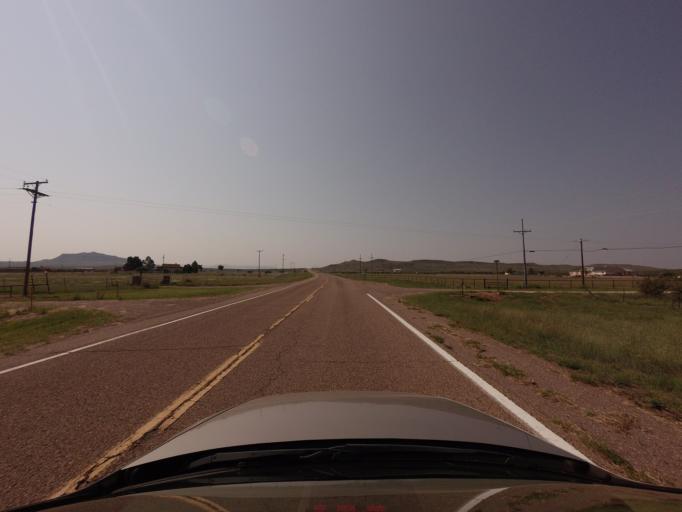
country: US
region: New Mexico
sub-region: Quay County
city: Tucumcari
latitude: 35.1249
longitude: -103.7286
